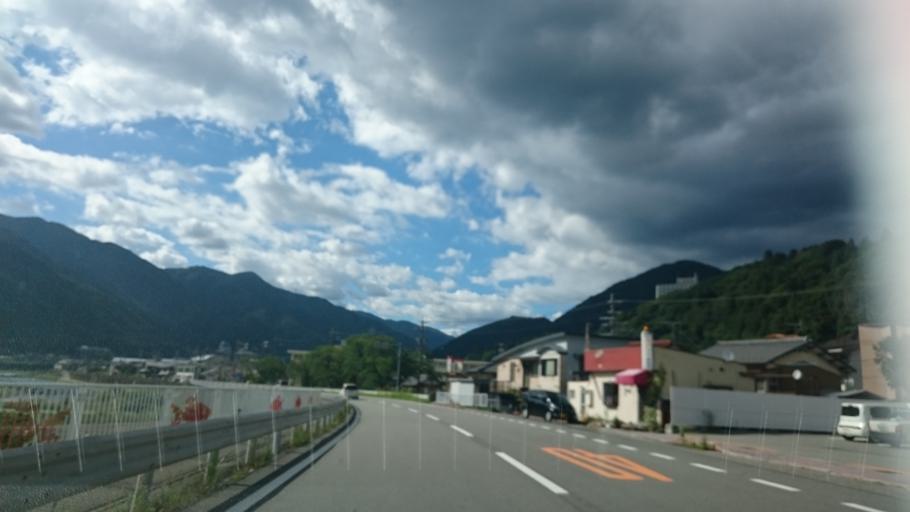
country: JP
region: Gifu
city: Gujo
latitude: 35.7977
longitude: 137.2540
